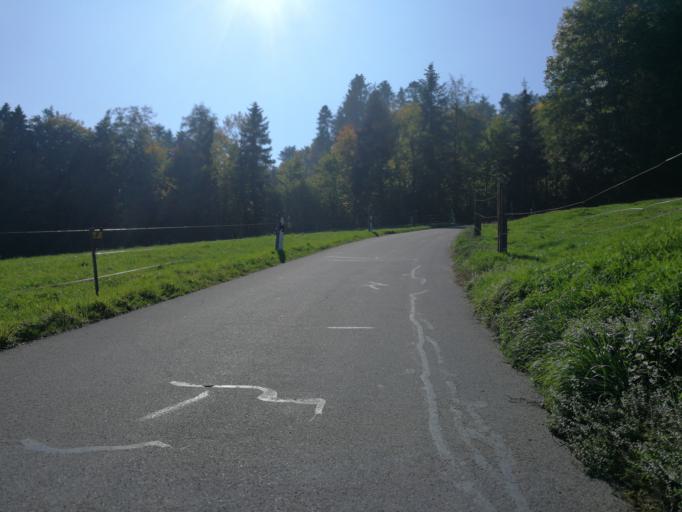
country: CH
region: Zurich
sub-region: Bezirk Uster
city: Hinteregg
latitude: 47.3222
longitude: 8.6779
